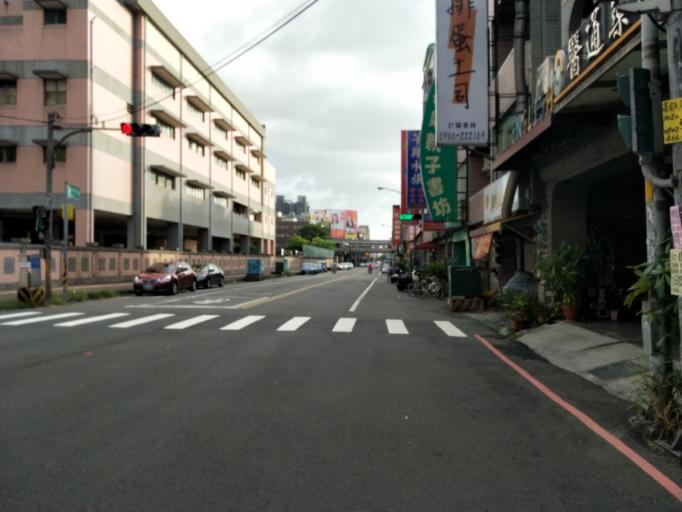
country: TW
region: Taiwan
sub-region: Hsinchu
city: Zhubei
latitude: 24.8320
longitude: 121.0053
